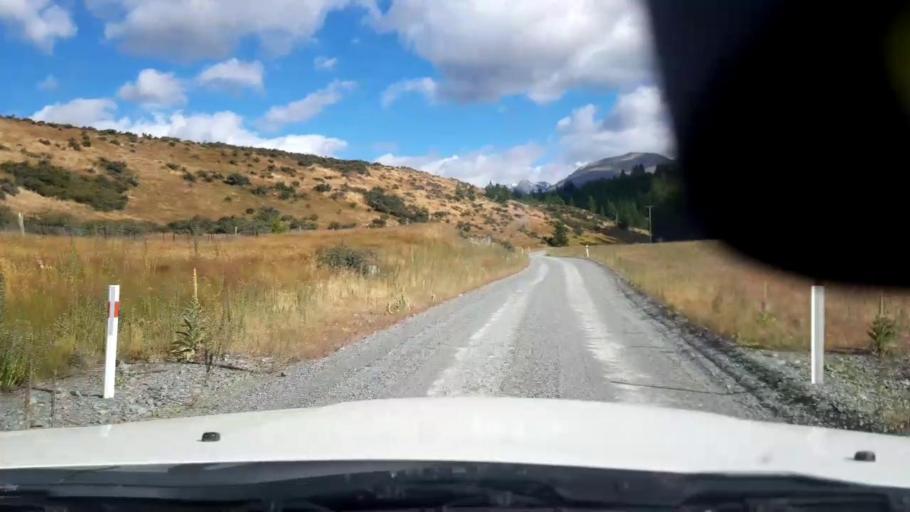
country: NZ
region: Canterbury
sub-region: Timaru District
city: Pleasant Point
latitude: -43.8764
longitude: 170.4646
